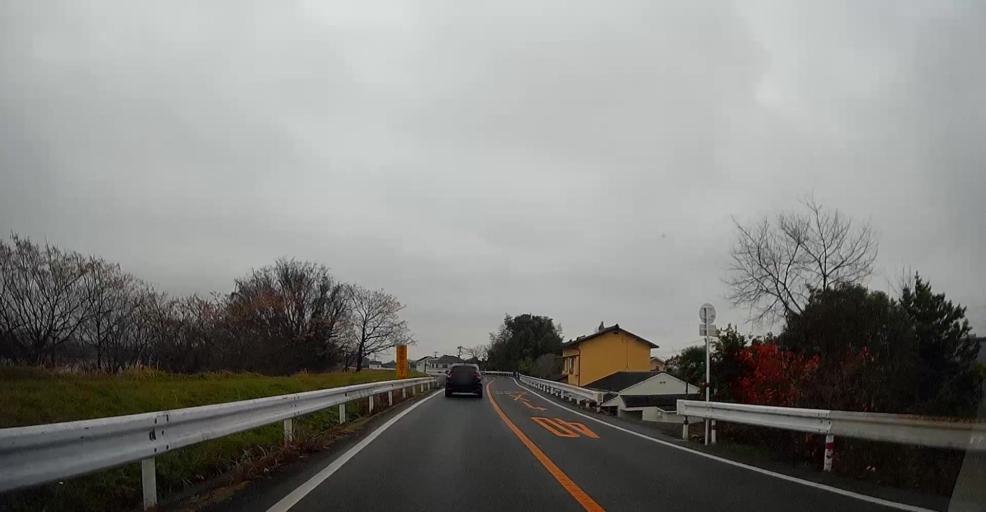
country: JP
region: Kumamoto
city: Kumamoto
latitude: 32.7575
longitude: 130.7500
